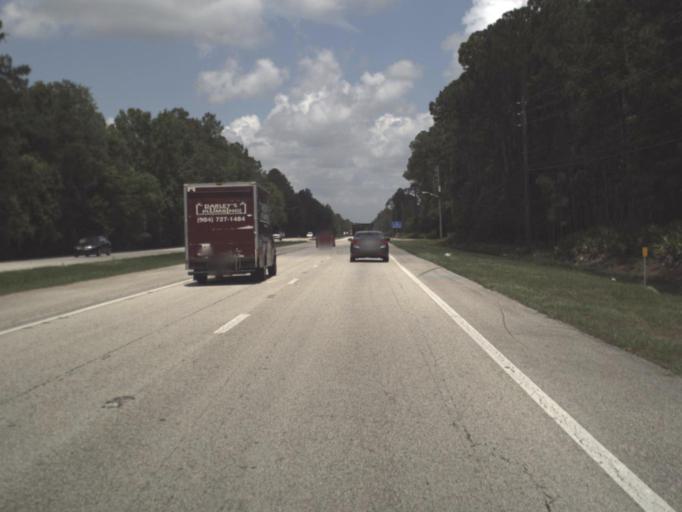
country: US
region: Florida
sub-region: Saint Johns County
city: Palm Valley
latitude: 30.1119
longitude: -81.4862
